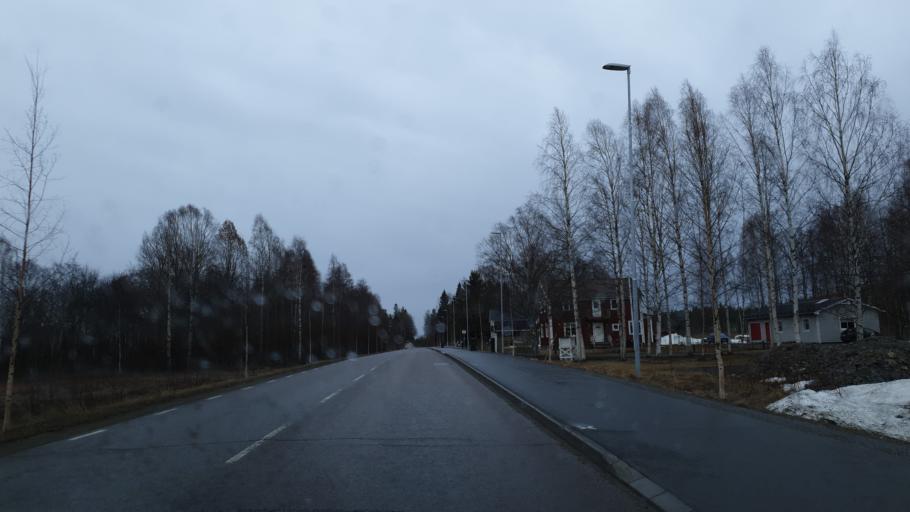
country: SE
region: Vaesterbotten
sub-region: Skelleftea Kommun
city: Kage
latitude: 64.8305
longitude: 21.0025
